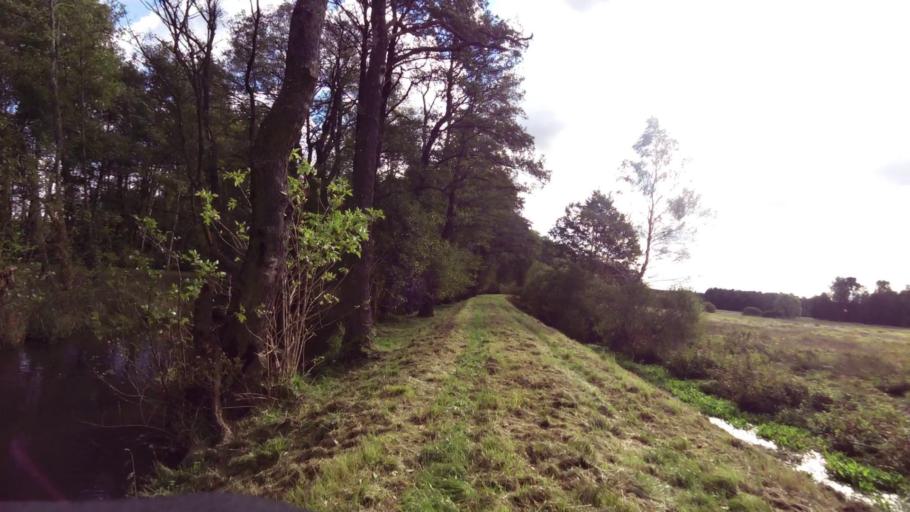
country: PL
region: West Pomeranian Voivodeship
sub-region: Powiat bialogardzki
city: Bialogard
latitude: 53.9970
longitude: 16.0328
